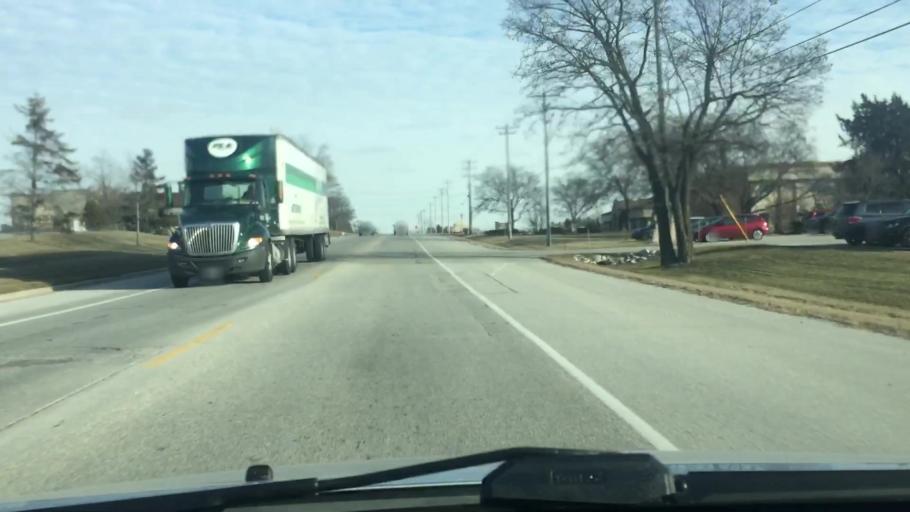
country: US
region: Wisconsin
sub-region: Waukesha County
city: Sussex
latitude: 43.1120
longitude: -88.2170
